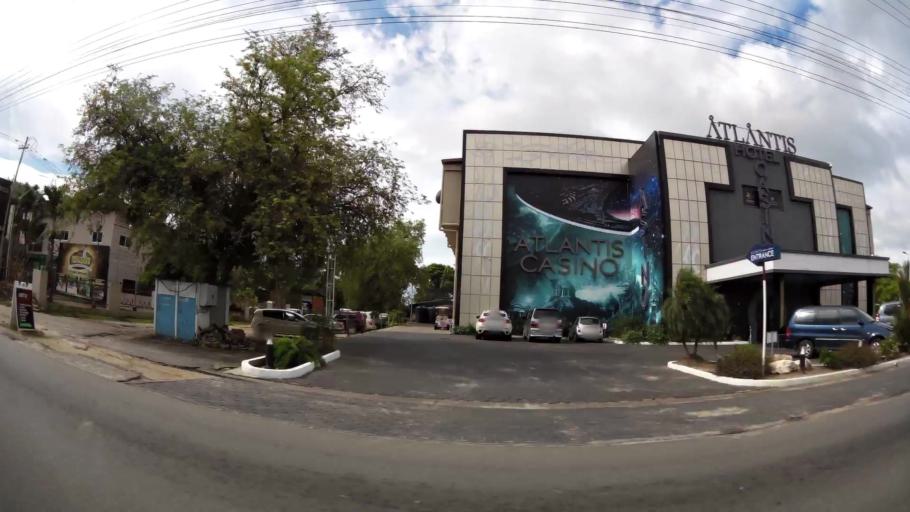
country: SR
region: Paramaribo
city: Paramaribo
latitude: 5.8408
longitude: -55.1878
